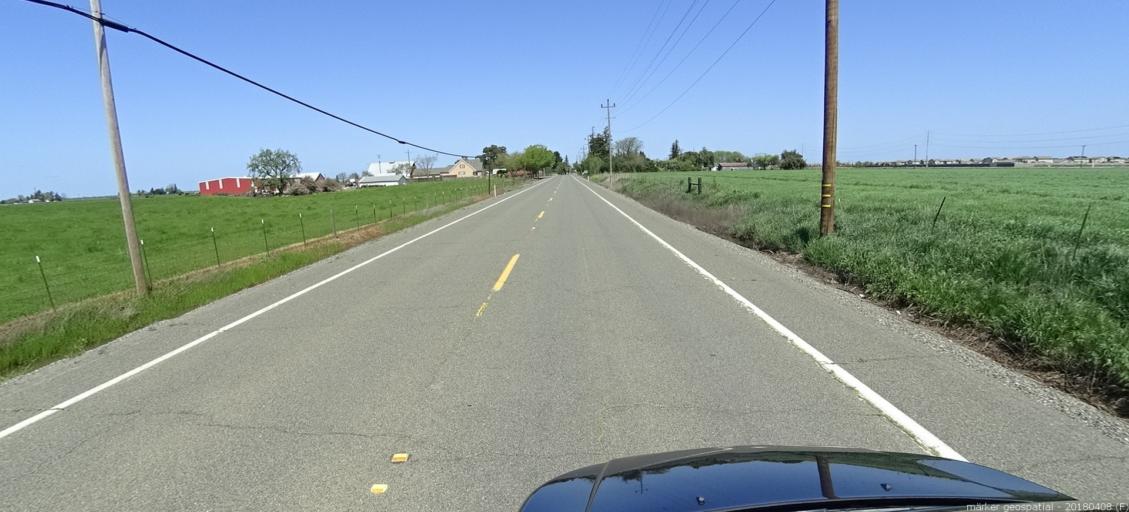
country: US
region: California
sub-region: Sacramento County
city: Laguna
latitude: 38.3685
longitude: -121.4542
